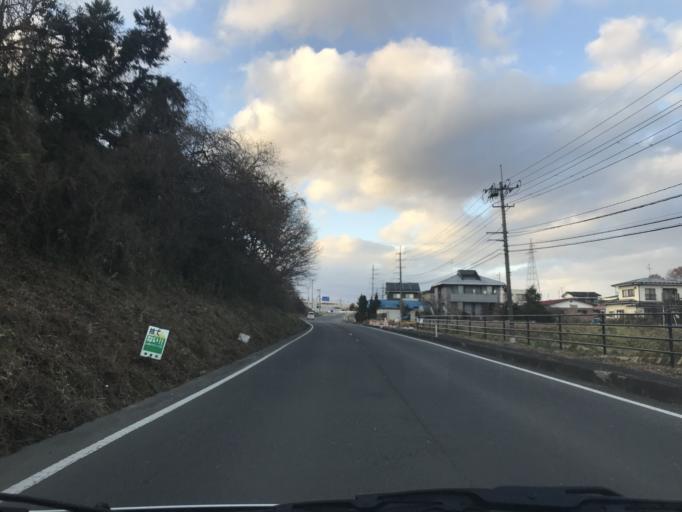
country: JP
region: Miyagi
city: Furukawa
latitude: 38.6675
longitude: 141.0105
